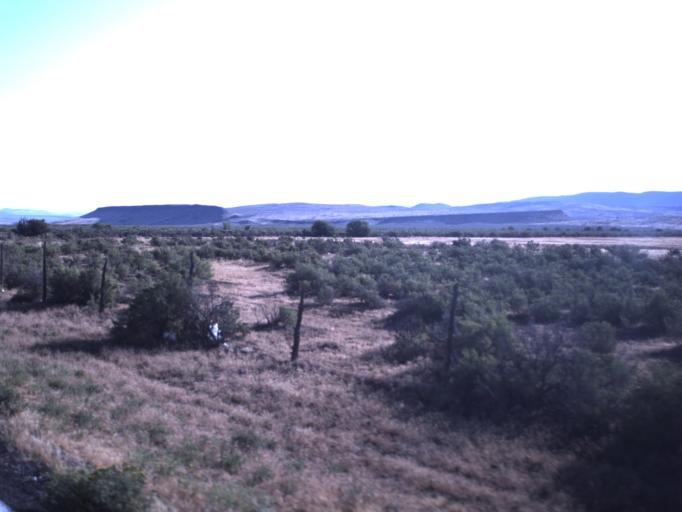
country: US
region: Utah
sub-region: Iron County
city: Enoch
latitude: 37.8171
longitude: -113.0504
